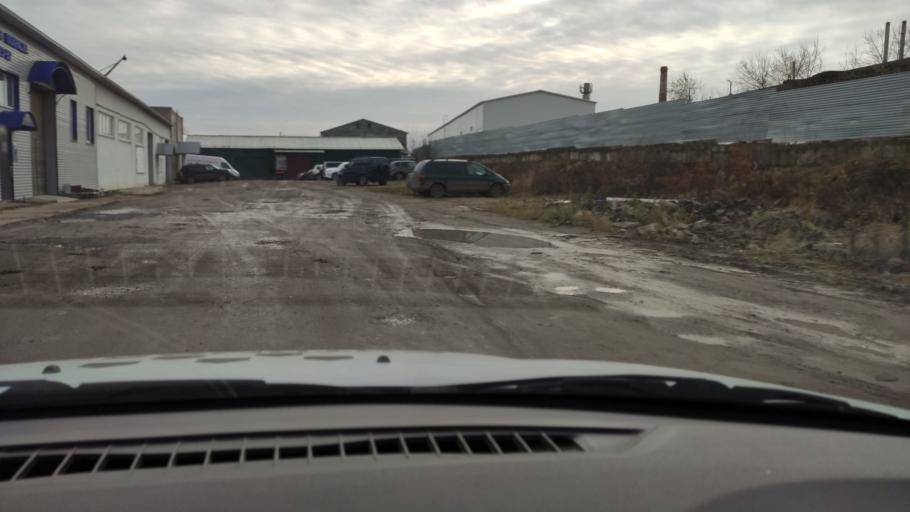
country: RU
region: Perm
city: Perm
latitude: 57.9583
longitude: 56.2168
